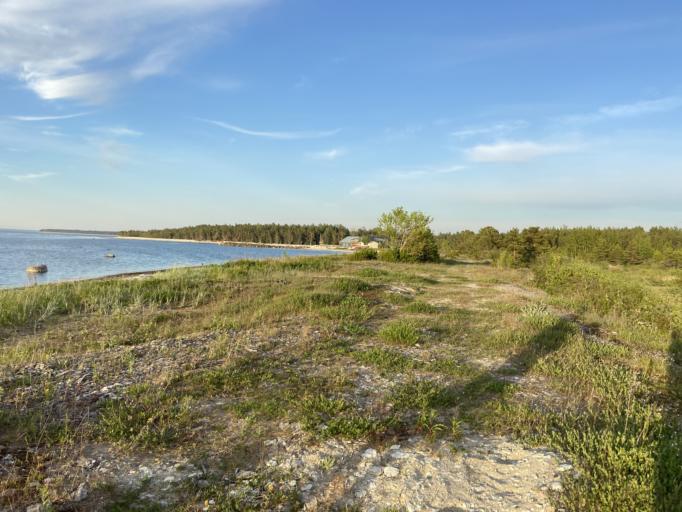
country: EE
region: Harju
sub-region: Paldiski linn
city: Paldiski
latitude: 59.2702
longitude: 23.7382
